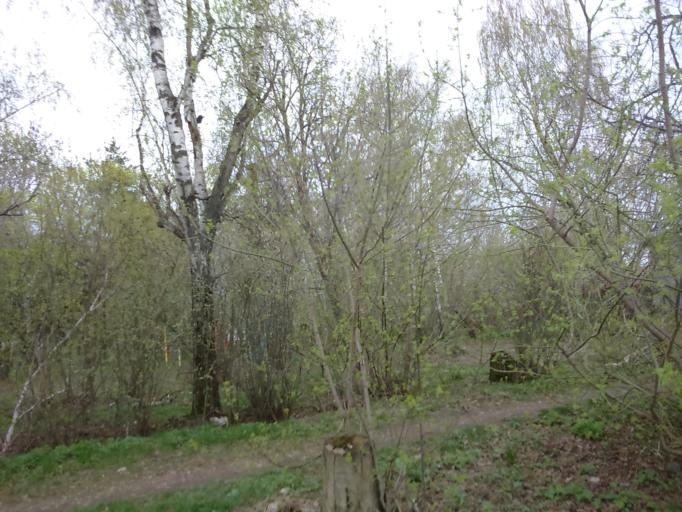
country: RU
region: Tula
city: Krapivna
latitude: 53.9403
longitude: 37.1534
